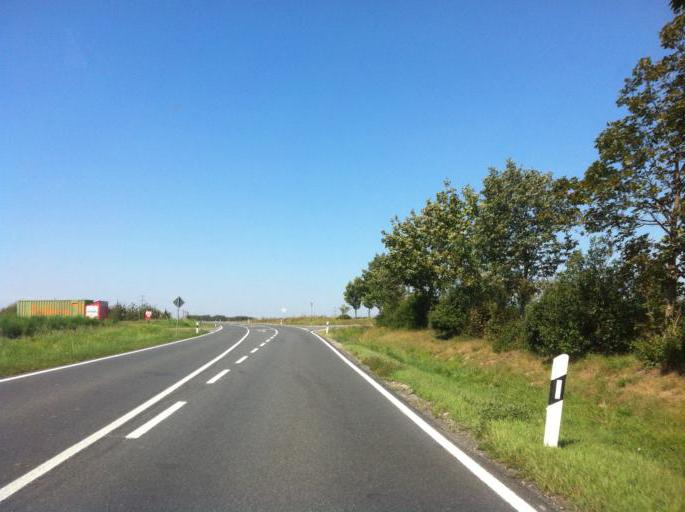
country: DE
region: Thuringia
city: Dachwig
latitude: 51.0761
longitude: 10.8473
